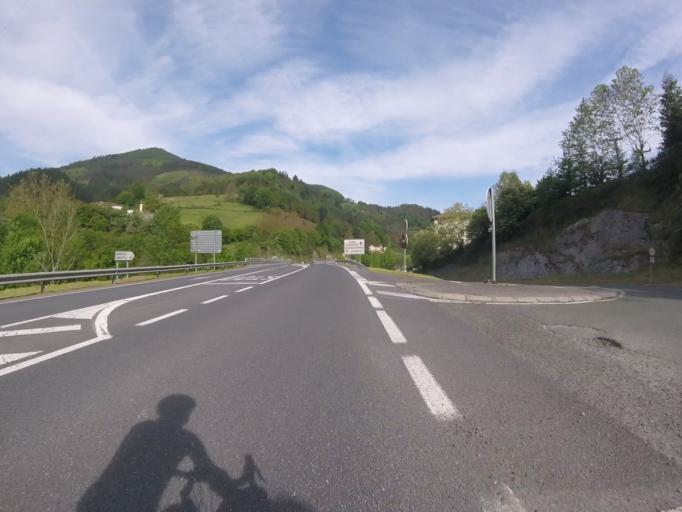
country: ES
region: Basque Country
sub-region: Provincia de Guipuzcoa
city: Urretxu
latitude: 43.0981
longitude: -2.3159
